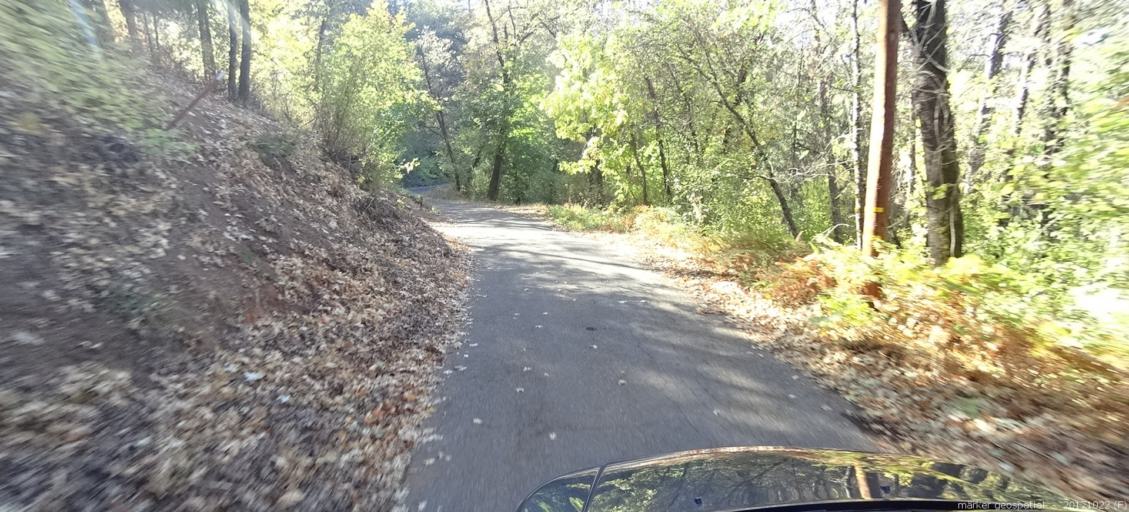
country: US
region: California
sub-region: Shasta County
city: Shasta Lake
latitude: 40.8393
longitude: -122.3635
